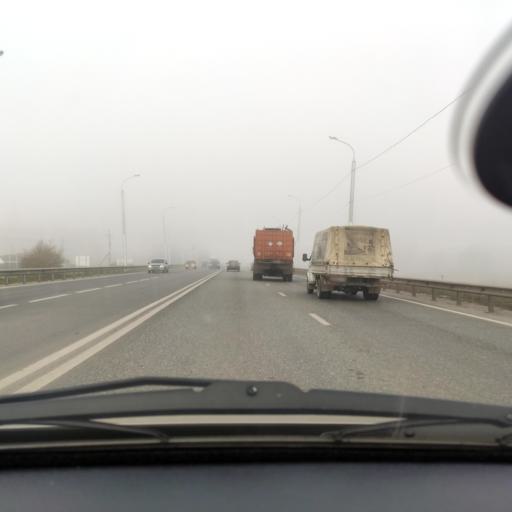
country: RU
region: Bashkortostan
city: Ufa
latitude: 54.8072
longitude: 56.1741
